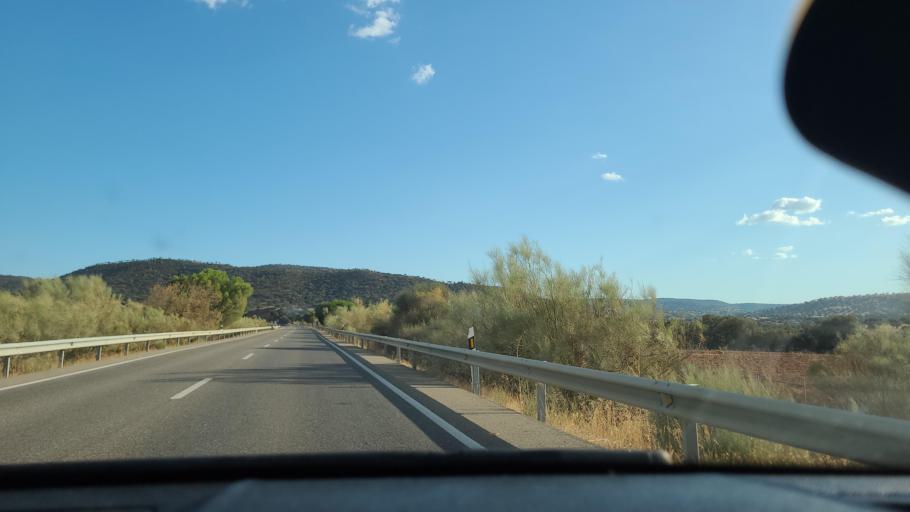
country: ES
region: Andalusia
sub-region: Province of Cordoba
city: Belmez
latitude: 38.2381
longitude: -5.1678
